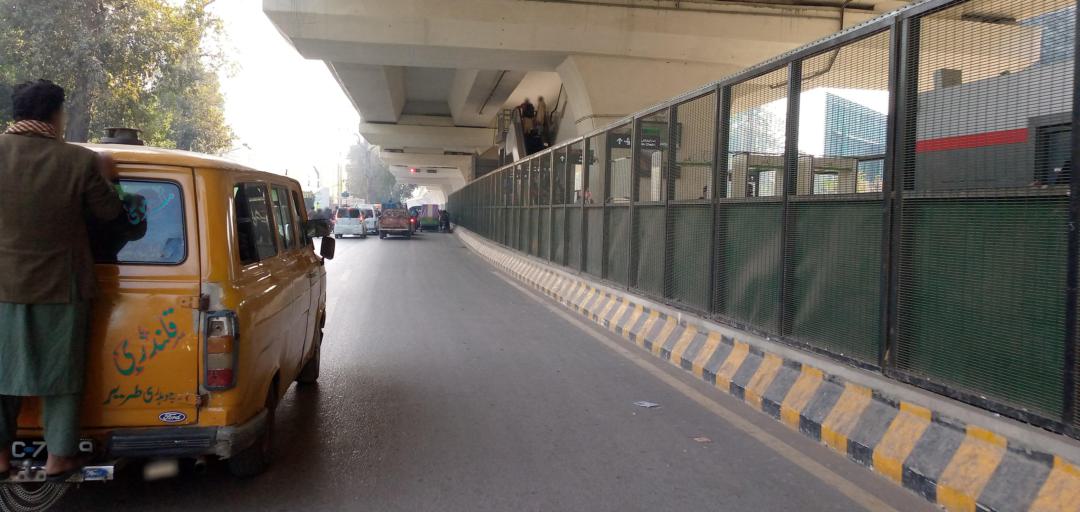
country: PK
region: Khyber Pakhtunkhwa
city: Peshawar
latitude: 33.9988
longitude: 71.5332
